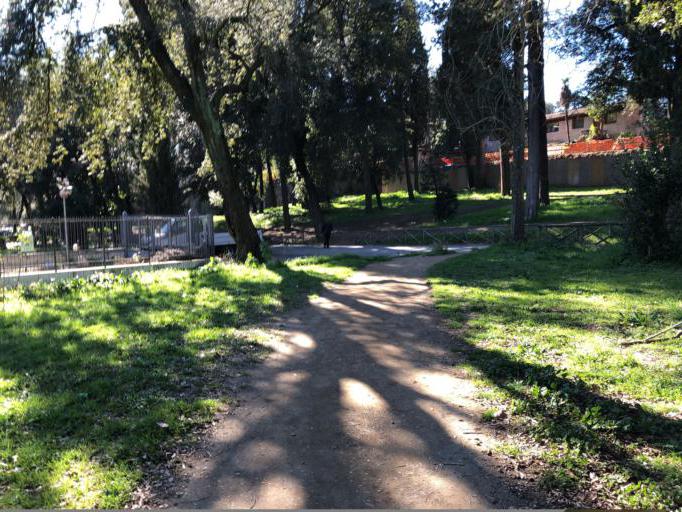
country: VA
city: Vatican City
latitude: 41.9150
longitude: 12.4798
